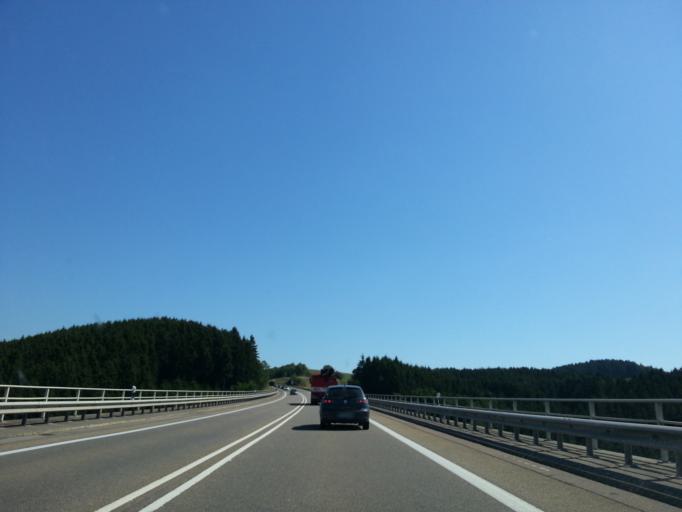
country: DE
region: Rheinland-Pfalz
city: Habscheid
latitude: 50.1999
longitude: 6.2836
